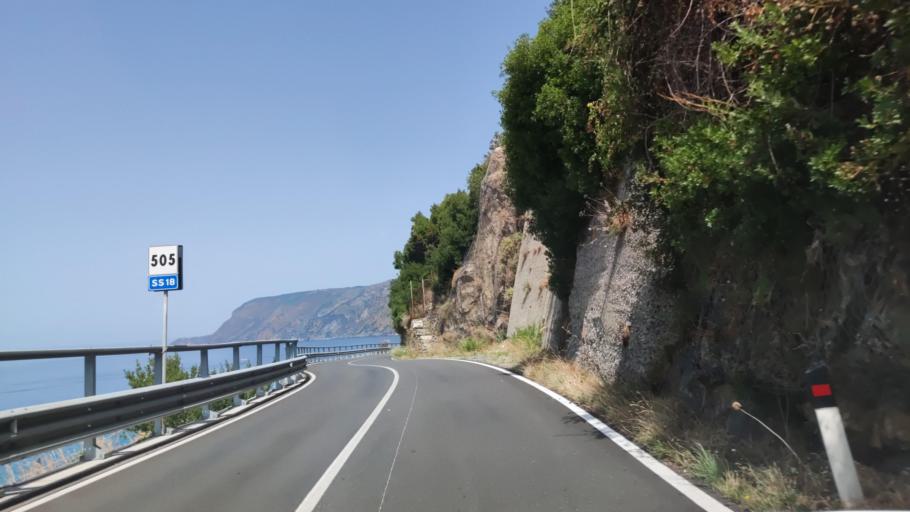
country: IT
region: Calabria
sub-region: Provincia di Reggio Calabria
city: Bagnara Calabra
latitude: 38.2753
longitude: 15.7860
